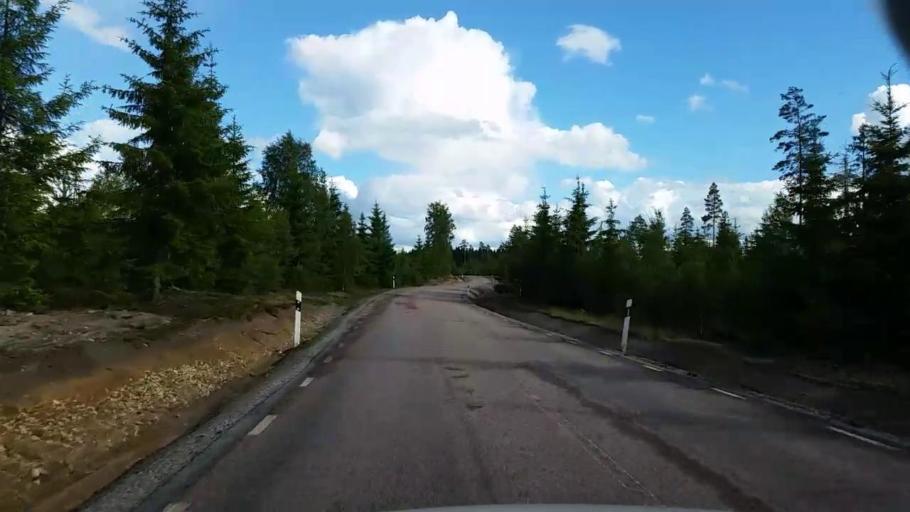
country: SE
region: Vaestmanland
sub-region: Fagersta Kommun
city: Fagersta
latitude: 59.8909
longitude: 15.8245
